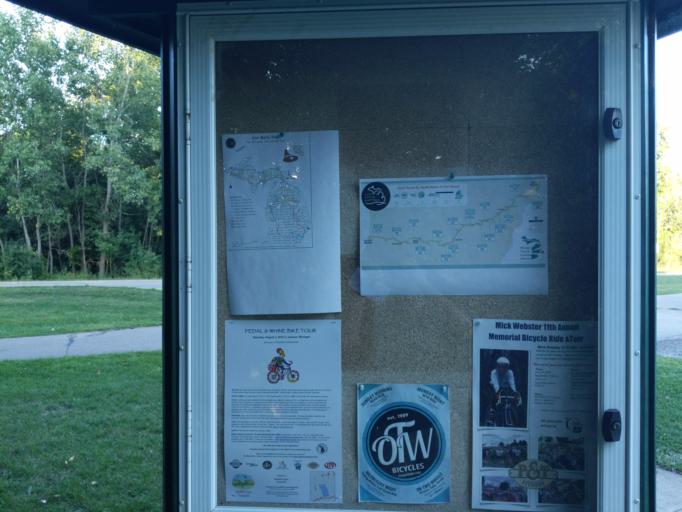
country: US
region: Michigan
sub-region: Jackson County
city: Vandercook Lake
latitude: 42.2082
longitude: -84.4392
